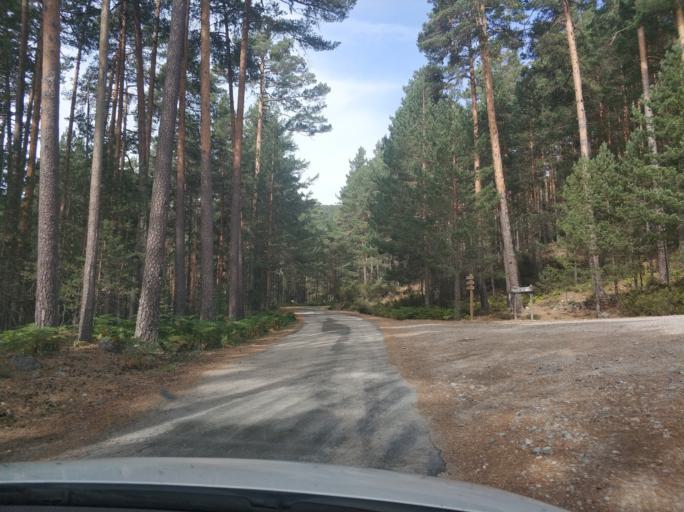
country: ES
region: Castille and Leon
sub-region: Provincia de Soria
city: Duruelo de la Sierra
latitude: 41.9950
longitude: -2.9200
